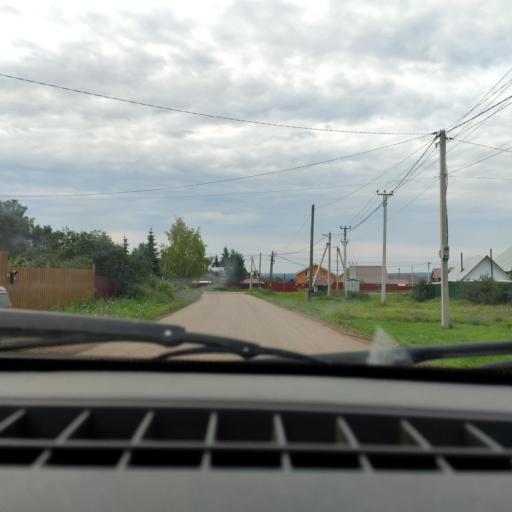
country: RU
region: Bashkortostan
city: Avdon
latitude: 54.6554
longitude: 55.7762
